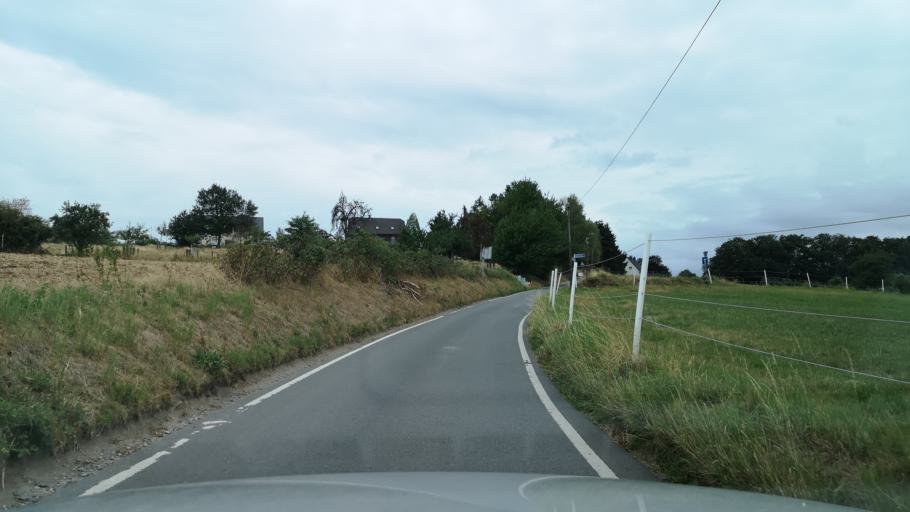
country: DE
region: North Rhine-Westphalia
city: Hattingen
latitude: 51.3942
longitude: 7.1184
